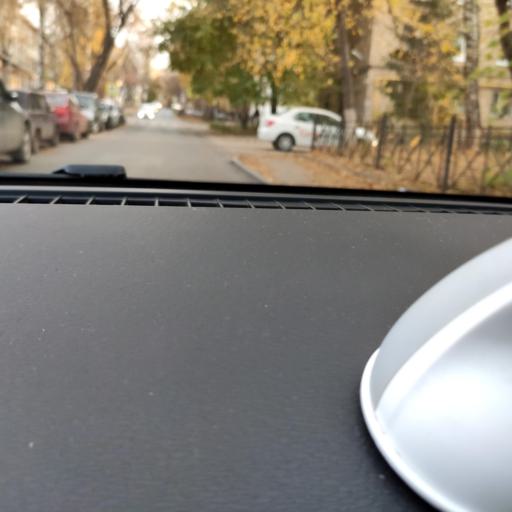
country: RU
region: Samara
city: Samara
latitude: 53.2104
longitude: 50.1269
